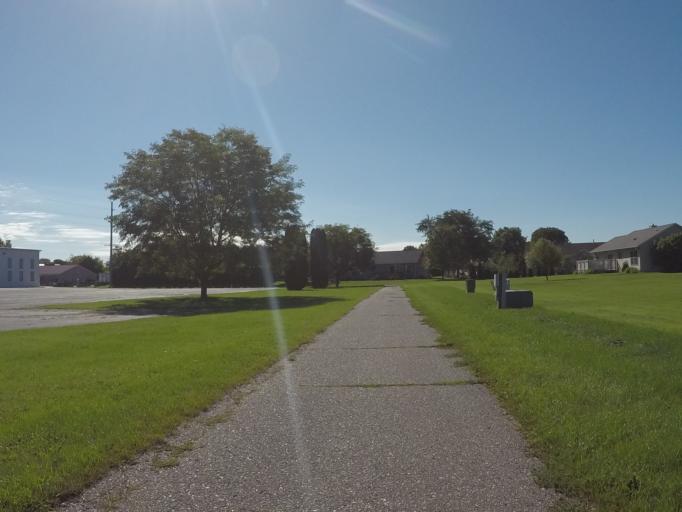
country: US
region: Wisconsin
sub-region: Richland County
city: Richland Center
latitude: 43.3228
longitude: -90.3827
